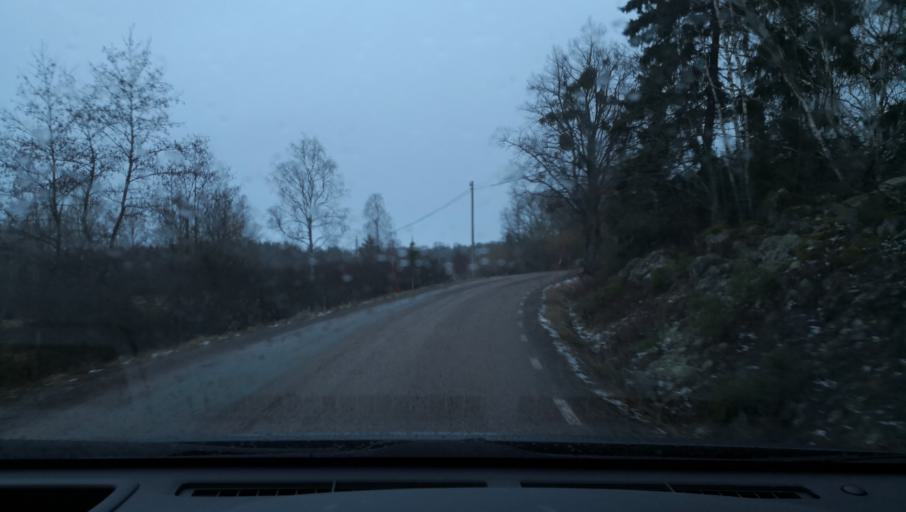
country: SE
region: Uppsala
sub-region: Enkopings Kommun
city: Hummelsta
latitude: 59.4614
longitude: 16.8421
